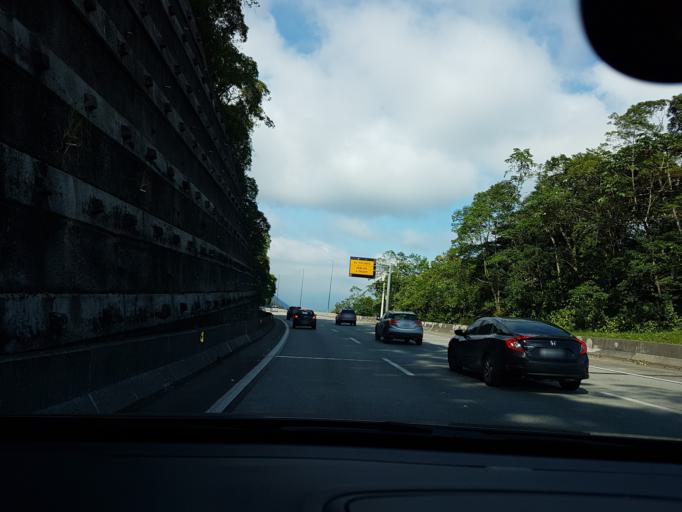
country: BR
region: Sao Paulo
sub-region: Cubatao
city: Cubatao
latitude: -23.9244
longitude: -46.5342
